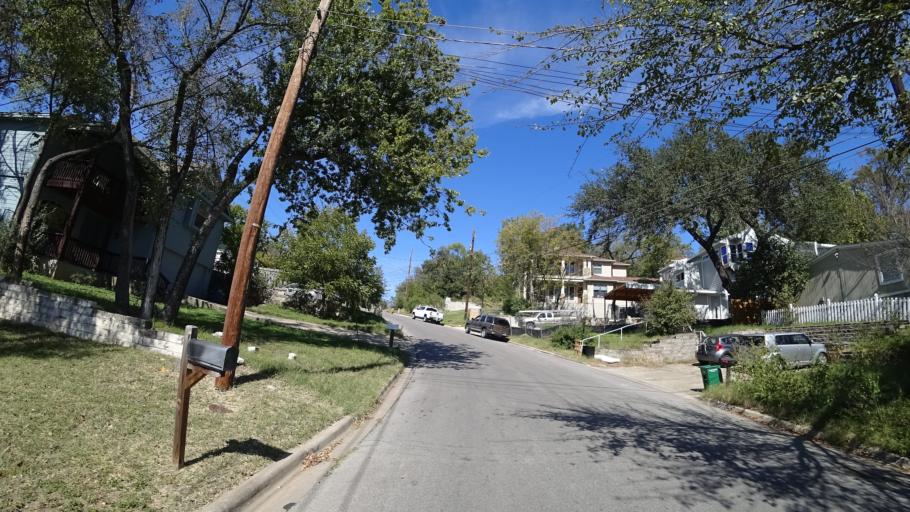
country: US
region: Texas
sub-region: Travis County
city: Austin
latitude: 30.2722
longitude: -97.6856
